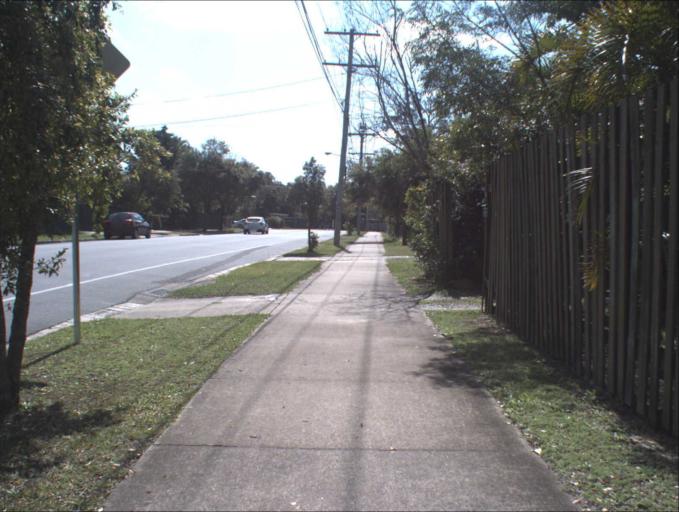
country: AU
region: Queensland
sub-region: Logan
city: Waterford West
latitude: -27.6740
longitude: 153.1113
